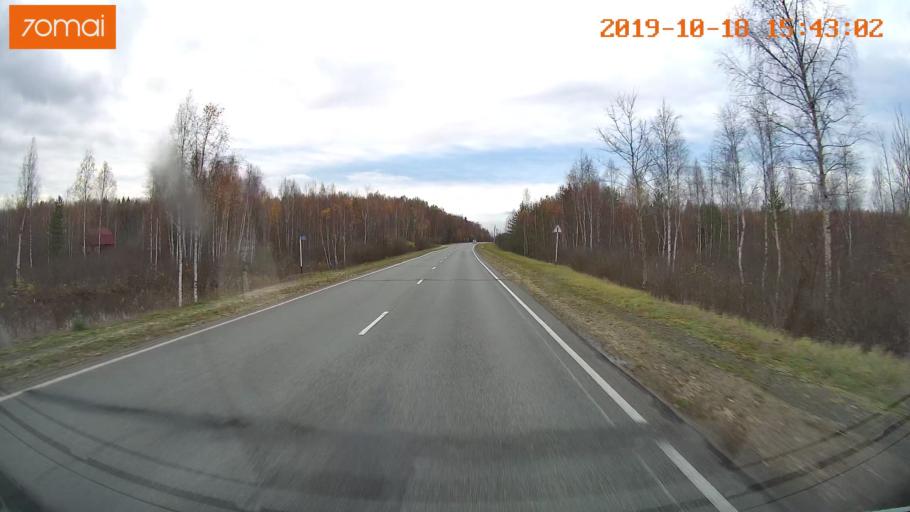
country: RU
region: Vladimir
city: Golovino
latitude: 55.9620
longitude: 40.5576
